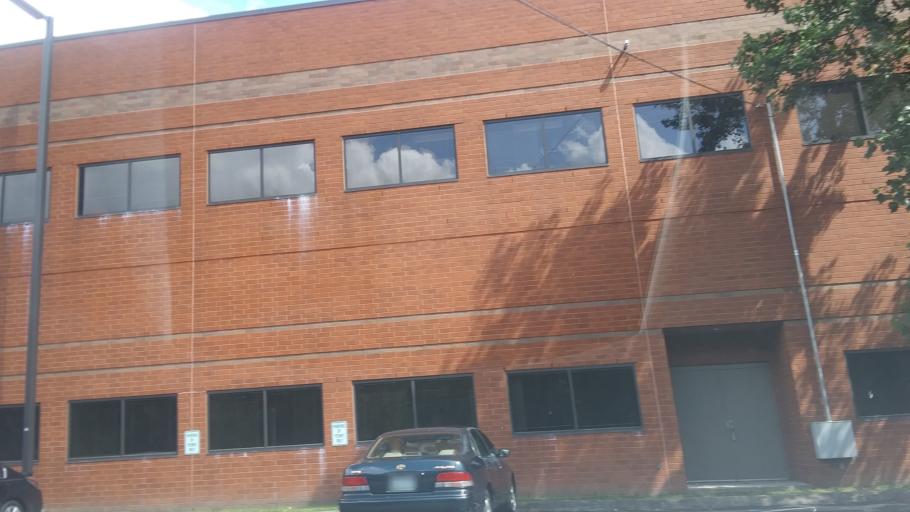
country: US
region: Tennessee
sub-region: Davidson County
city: Oak Hill
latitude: 36.0949
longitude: -86.7030
